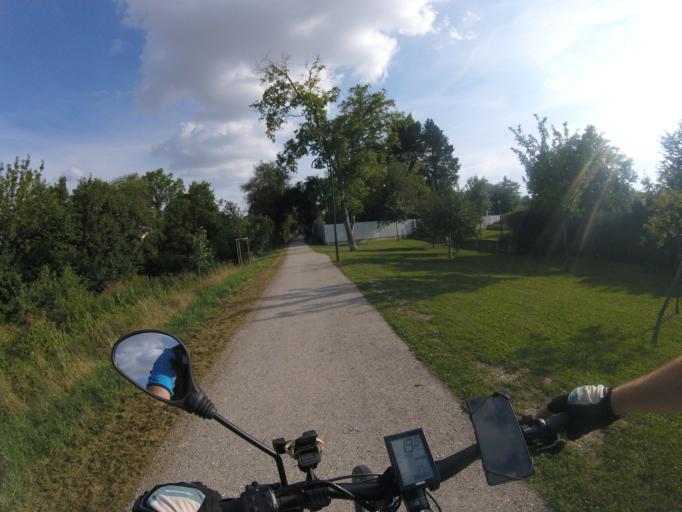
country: AT
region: Lower Austria
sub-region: Politischer Bezirk Baden
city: Trumau
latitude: 47.9970
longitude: 16.3492
